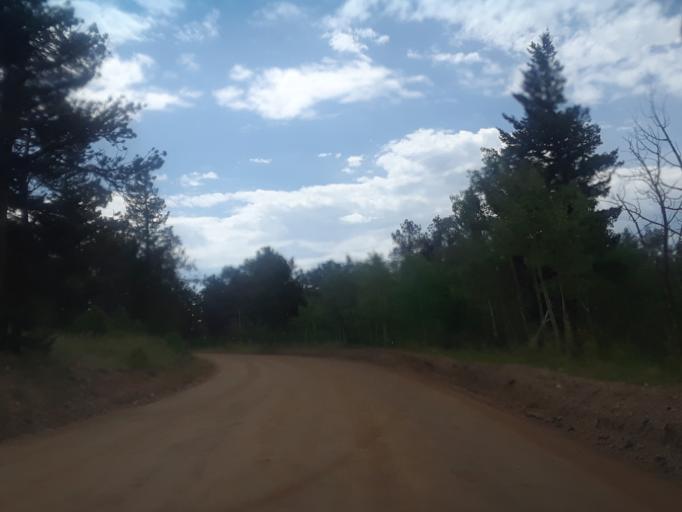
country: US
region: Colorado
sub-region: Boulder County
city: Nederland
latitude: 40.0595
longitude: -105.4317
